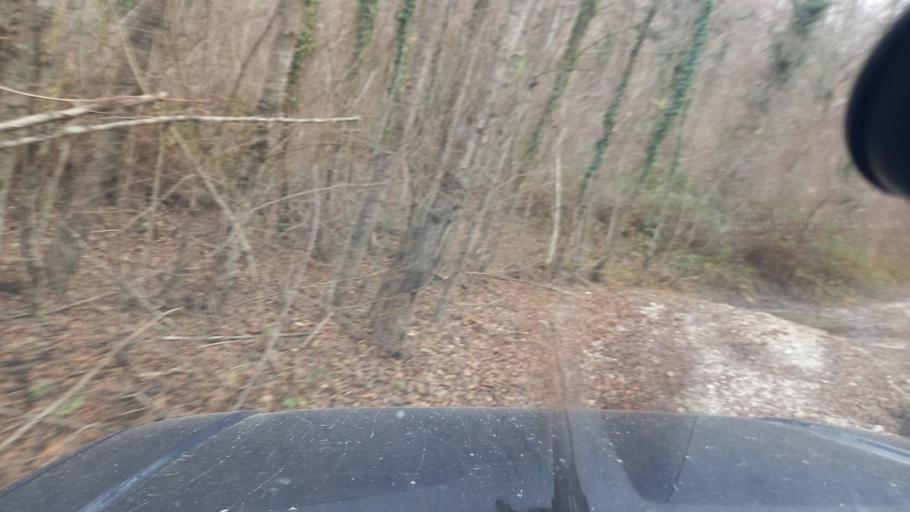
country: RU
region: Krasnodarskiy
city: Pshada
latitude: 44.4924
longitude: 38.4197
